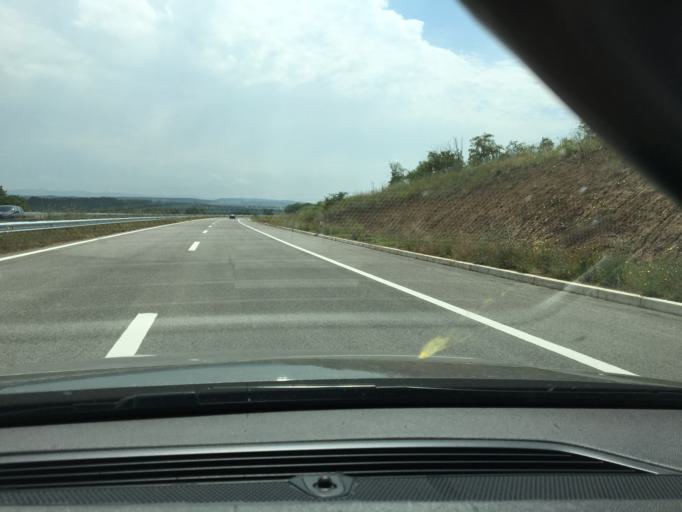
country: MK
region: Sveti Nikole
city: Gorobinci
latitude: 41.9132
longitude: 21.8919
